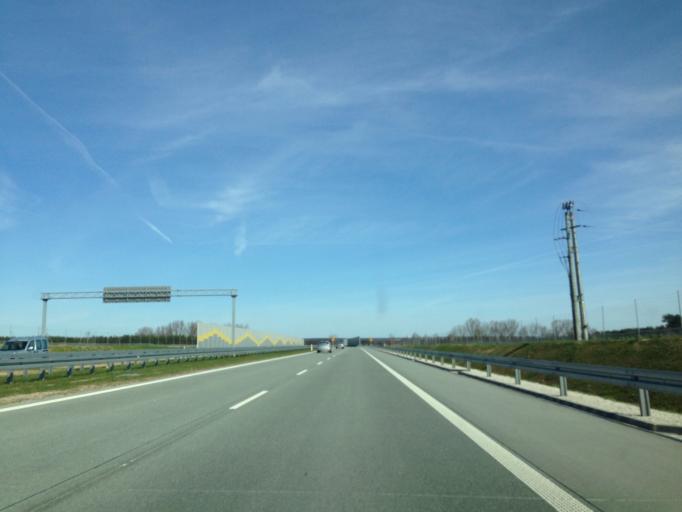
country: PL
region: Lodz Voivodeship
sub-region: Powiat sieradzki
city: Sieradz
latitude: 51.5614
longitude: 18.7476
